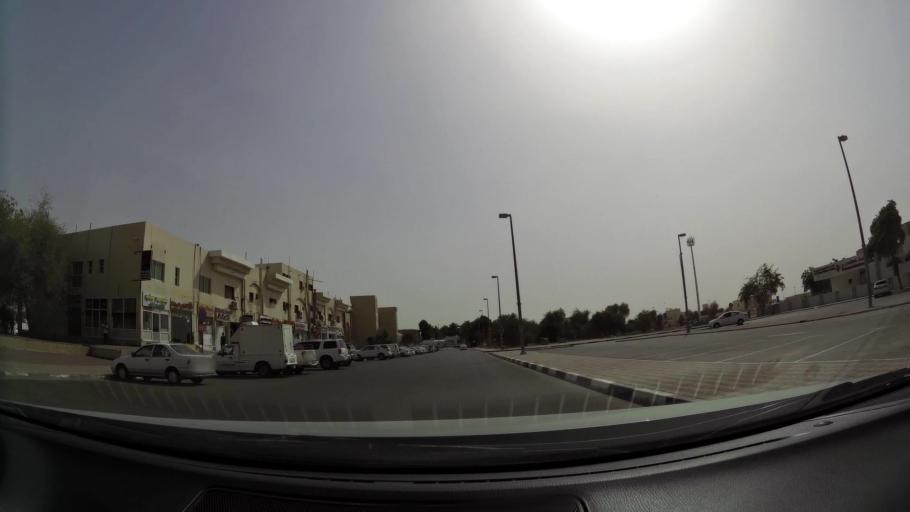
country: AE
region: Abu Dhabi
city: Al Ain
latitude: 24.1852
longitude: 55.6278
